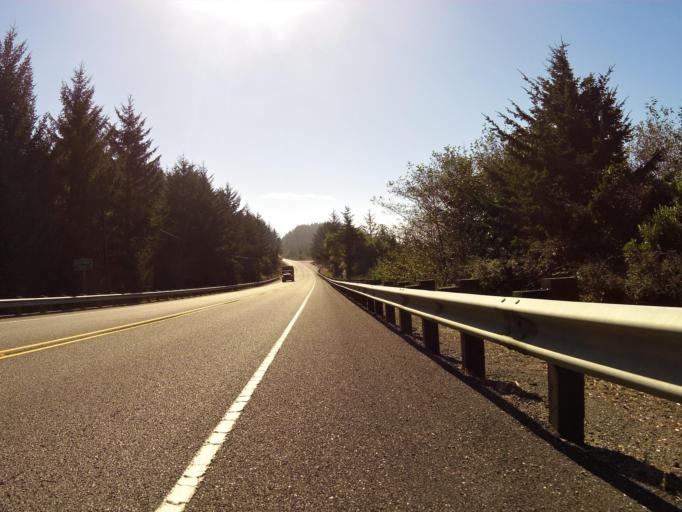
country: US
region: Oregon
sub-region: Curry County
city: Brookings
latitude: 42.1017
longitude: -124.3445
